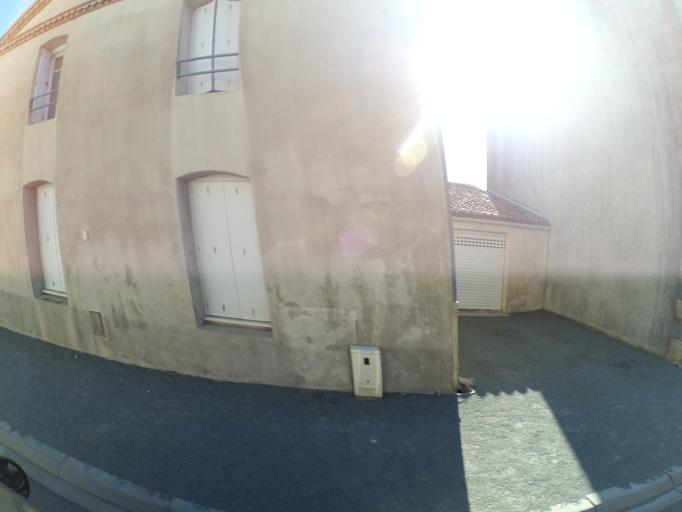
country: FR
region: Pays de la Loire
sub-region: Departement de la Vendee
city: Saint-Michel-Mont-Mercure
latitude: 46.8301
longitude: -0.8842
